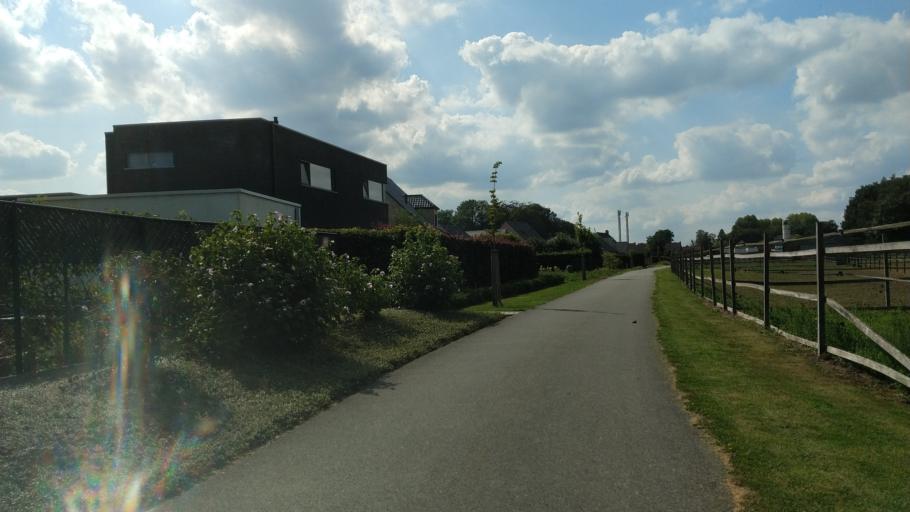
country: BE
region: Flanders
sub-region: Provincie Oost-Vlaanderen
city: Kaprijke
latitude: 51.2351
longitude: 3.6809
